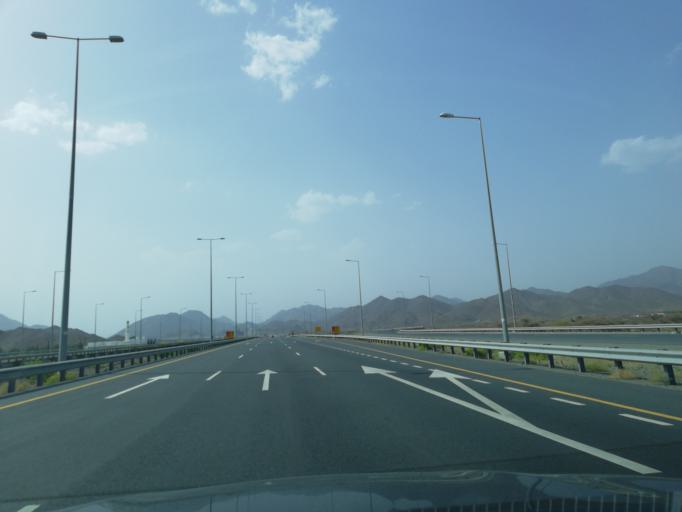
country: OM
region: Muhafazat ad Dakhiliyah
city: Sufalat Sama'il
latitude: 23.0809
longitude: 58.1838
